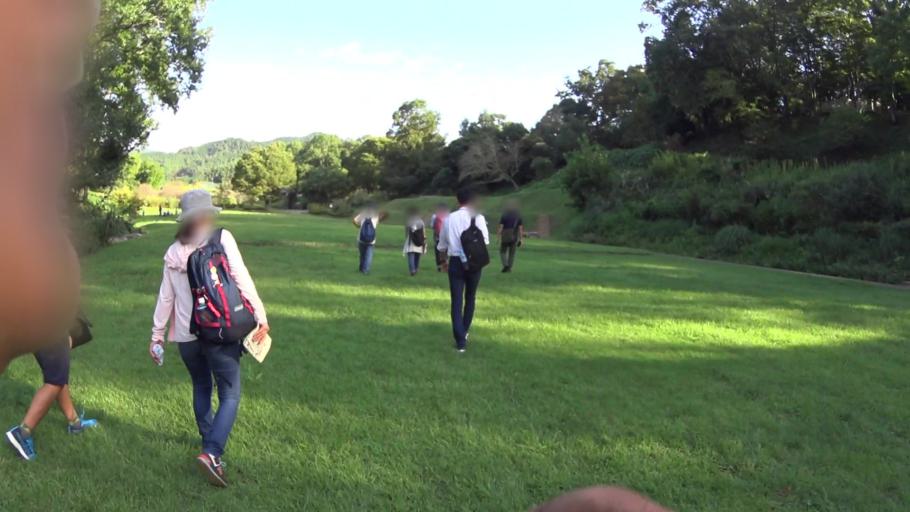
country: JP
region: Nara
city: Kashihara-shi
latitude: 34.4644
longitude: 135.8049
